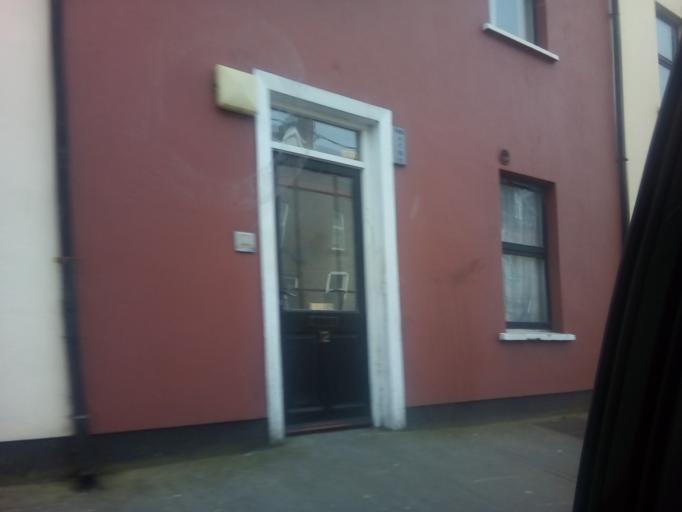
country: IE
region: Munster
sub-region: County Cork
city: Cork
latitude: 51.8936
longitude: -8.4853
